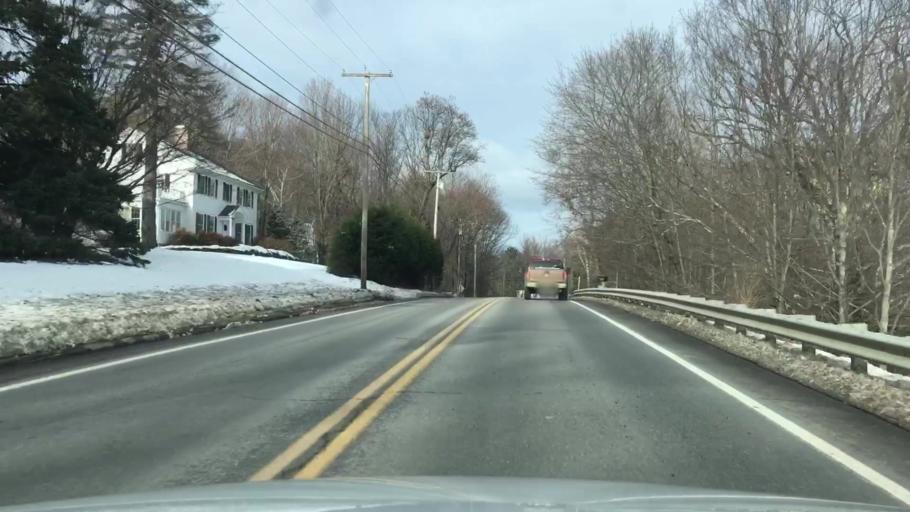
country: US
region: Maine
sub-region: Kennebec County
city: Winthrop
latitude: 44.3142
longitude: -69.9779
